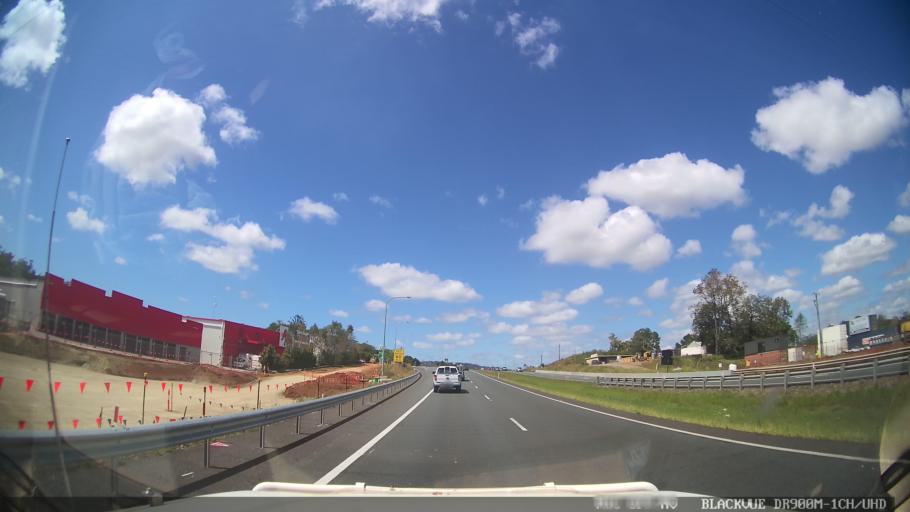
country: AU
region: Queensland
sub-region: Sunshine Coast
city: Woombye
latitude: -26.6814
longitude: 153.0029
